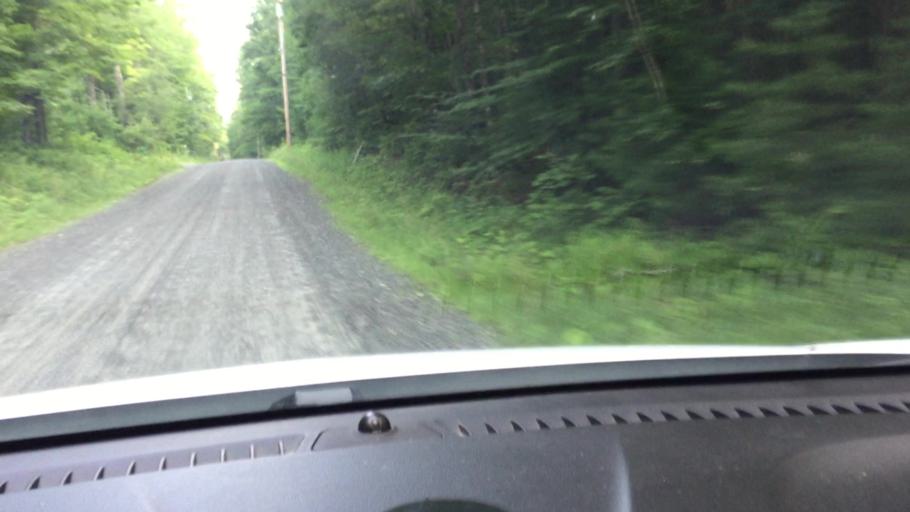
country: US
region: Massachusetts
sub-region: Berkshire County
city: Otis
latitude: 42.1975
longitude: -73.0642
